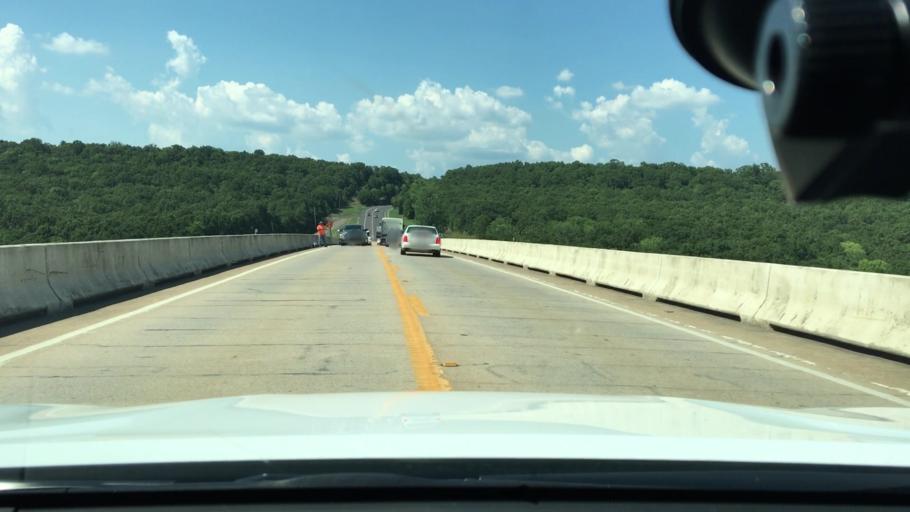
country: US
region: Arkansas
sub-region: Johnson County
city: Clarksville
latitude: 35.4113
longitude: -93.5321
